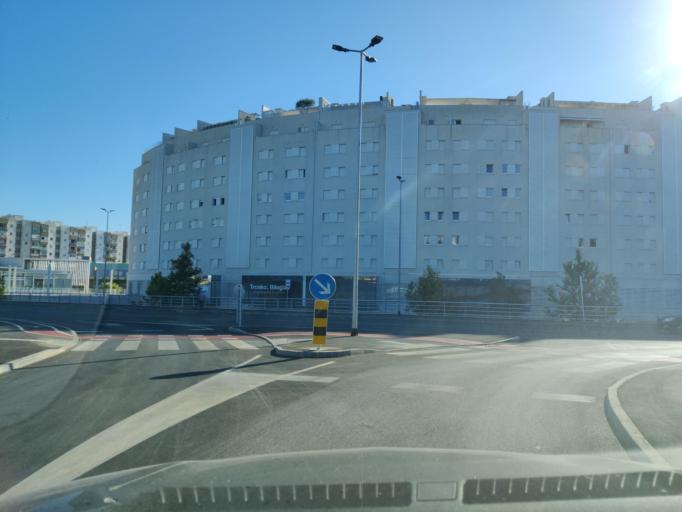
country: HR
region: Zadarska
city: Zadar
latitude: 44.1150
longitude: 15.2365
